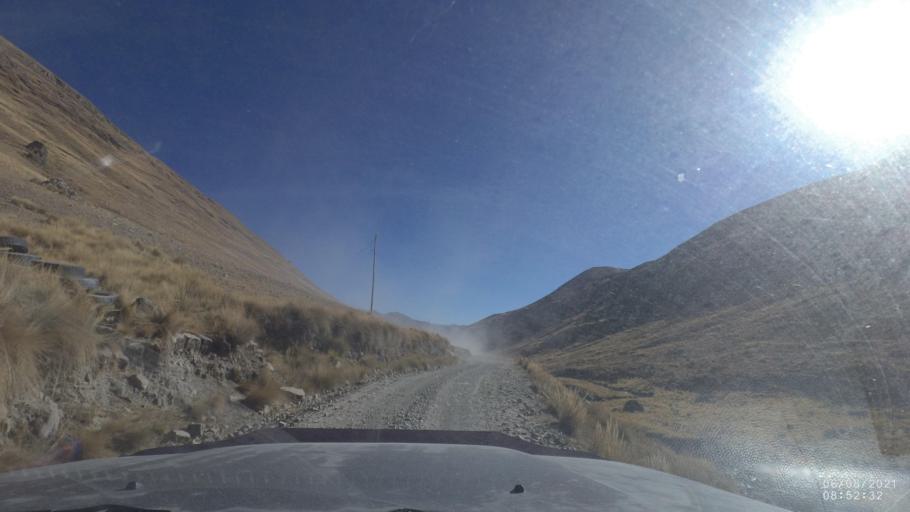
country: BO
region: Cochabamba
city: Sipe Sipe
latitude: -17.1369
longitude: -66.4403
